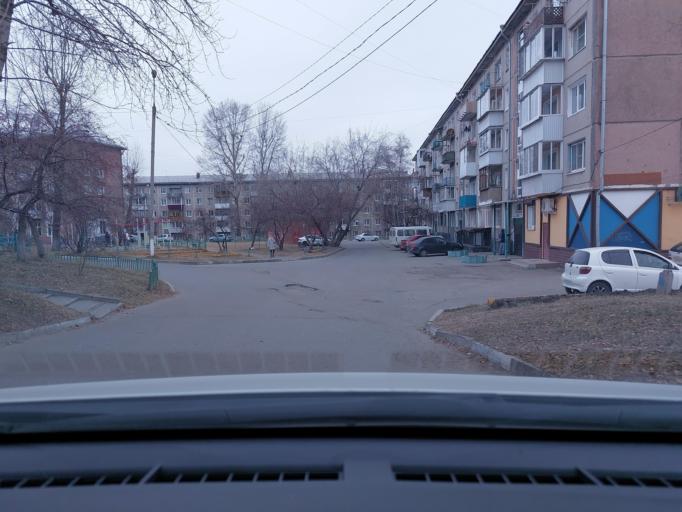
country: RU
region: Irkutsk
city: Smolenshchina
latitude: 52.3482
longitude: 104.1655
